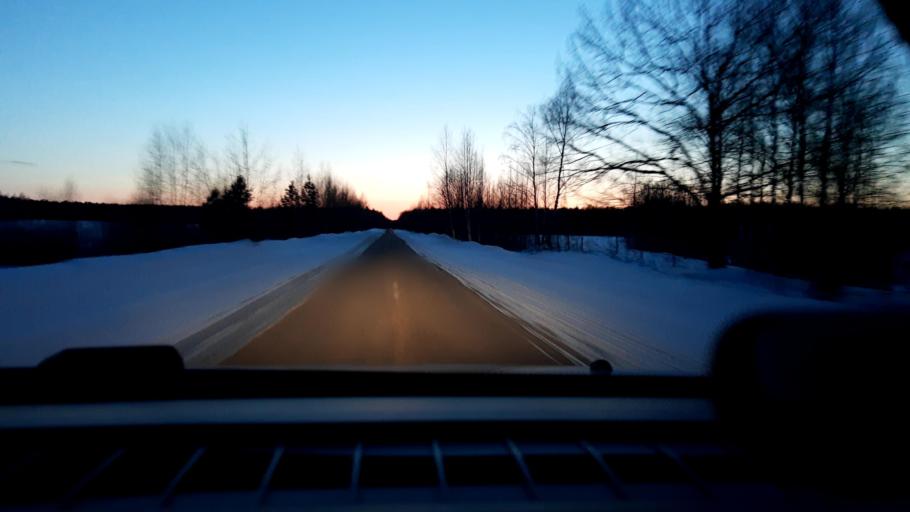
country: RU
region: Nizjnij Novgorod
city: Spasskoye
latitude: 56.1524
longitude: 45.4291
